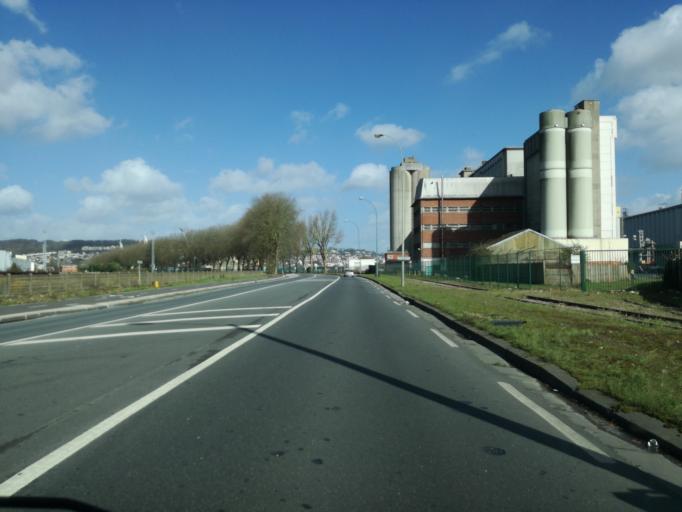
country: FR
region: Haute-Normandie
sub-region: Departement de la Seine-Maritime
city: Canteleu
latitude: 49.4392
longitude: 1.0399
